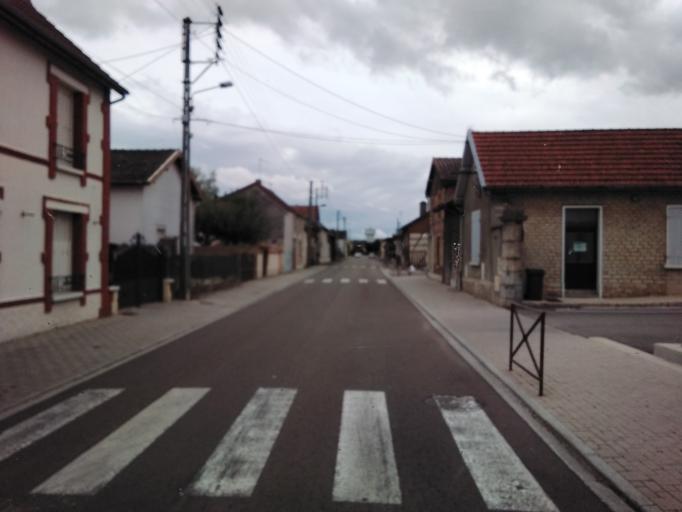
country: FR
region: Champagne-Ardenne
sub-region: Departement de l'Aube
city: Brienne-le-Chateau
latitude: 48.3890
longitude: 4.5286
